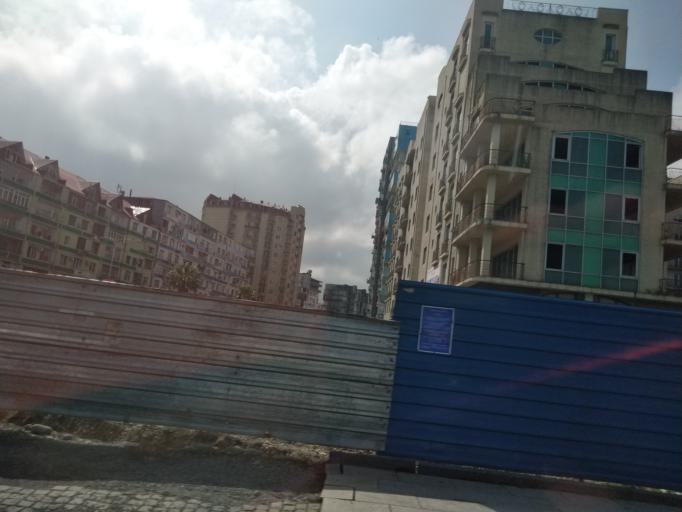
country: GE
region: Ajaria
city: Batumi
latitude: 41.6457
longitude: 41.6186
